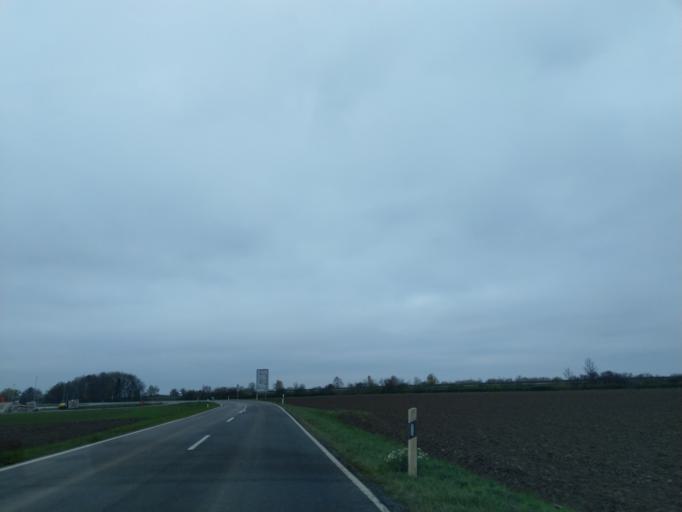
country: DE
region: Bavaria
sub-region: Lower Bavaria
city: Otzing
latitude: 48.7611
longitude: 12.7748
